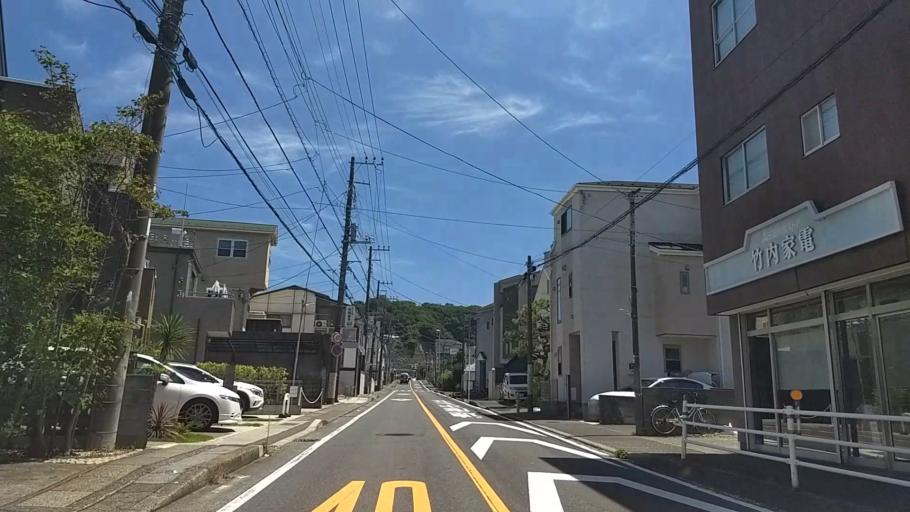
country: JP
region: Kanagawa
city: Kamakura
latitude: 35.3124
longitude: 139.5568
